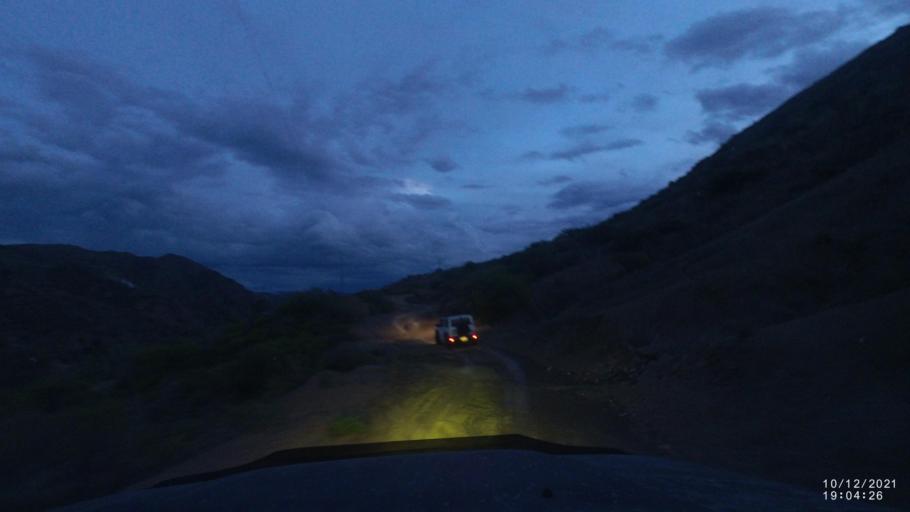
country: BO
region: Cochabamba
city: Tarata
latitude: -17.9024
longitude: -65.9421
